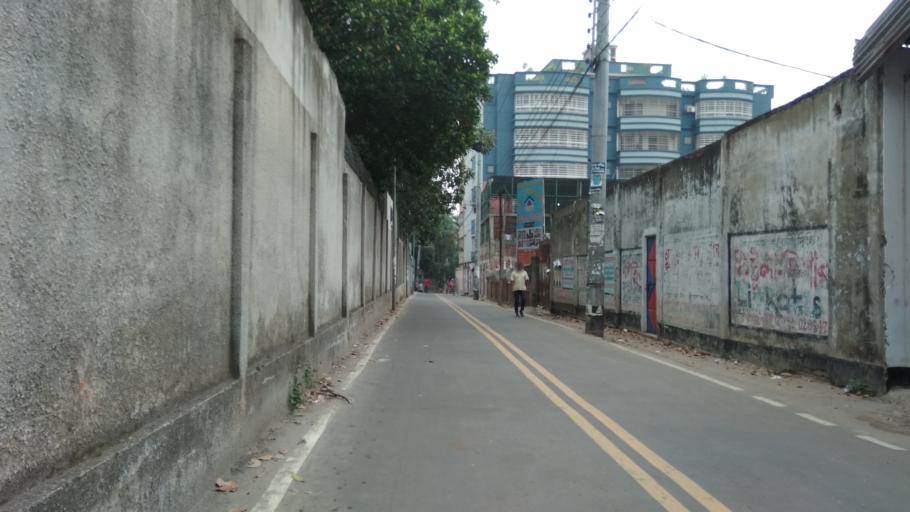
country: BD
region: Dhaka
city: Tungi
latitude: 23.8210
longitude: 90.3615
